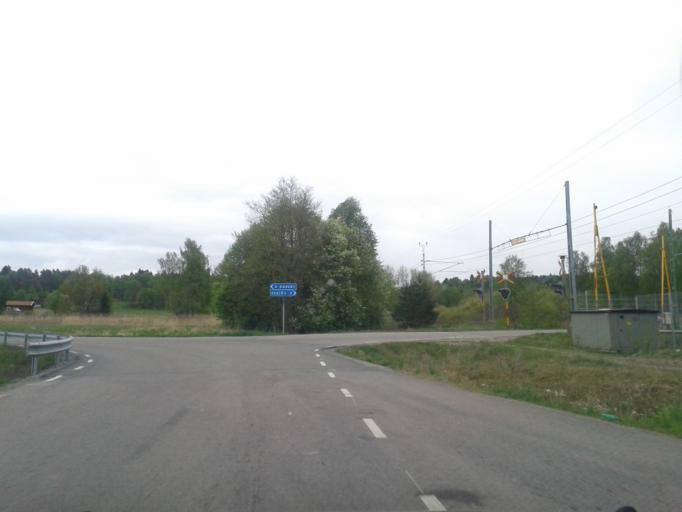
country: SE
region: Vaestra Goetaland
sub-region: Kungalvs Kommun
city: Kode
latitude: 57.9033
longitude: 11.8984
